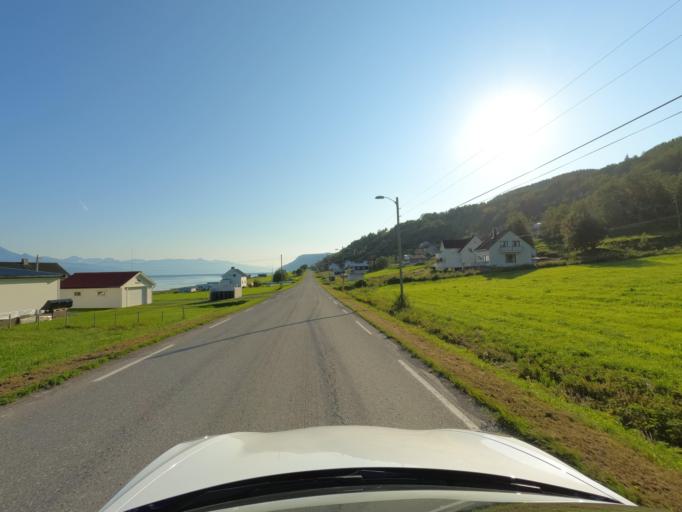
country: NO
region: Nordland
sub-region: Narvik
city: Bjerkvik
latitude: 68.5305
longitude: 17.4687
